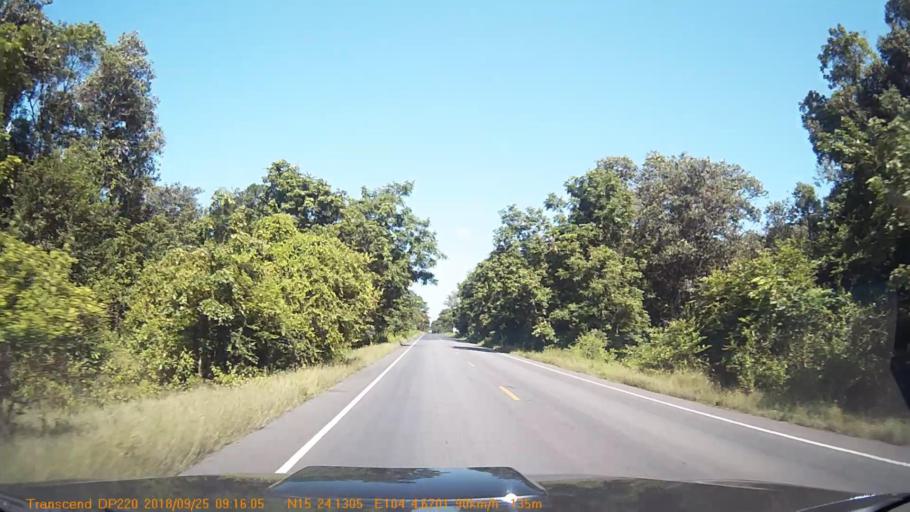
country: TH
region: Sisaket
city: Sila Lat
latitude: 15.4021
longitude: 104.0780
